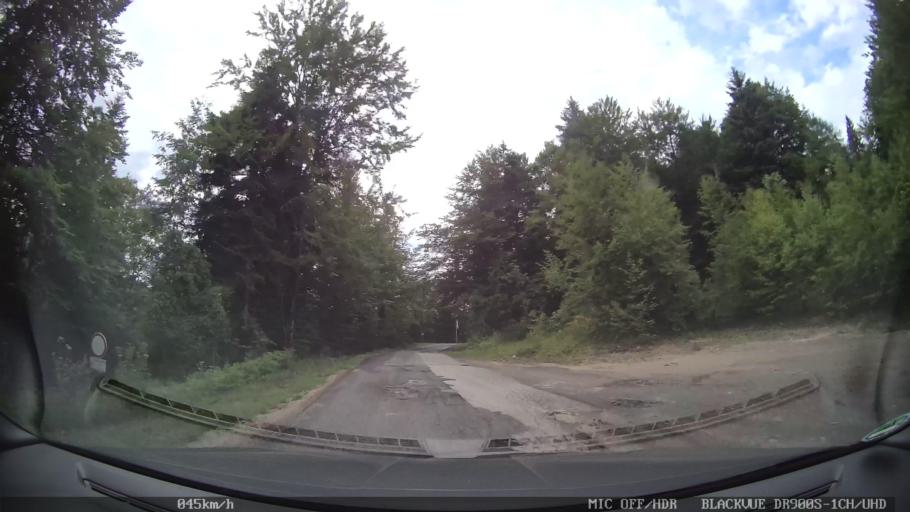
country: HR
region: Licko-Senjska
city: Jezerce
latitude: 44.9296
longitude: 15.5546
